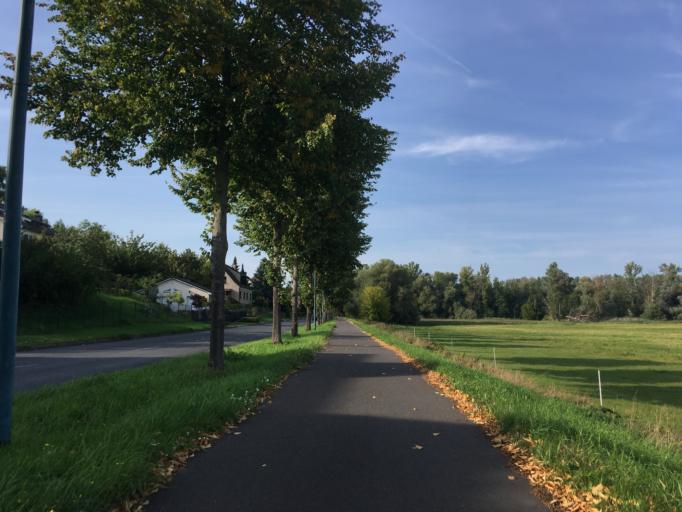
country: DE
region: Brandenburg
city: Frankfurt (Oder)
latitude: 52.3102
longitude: 14.5573
